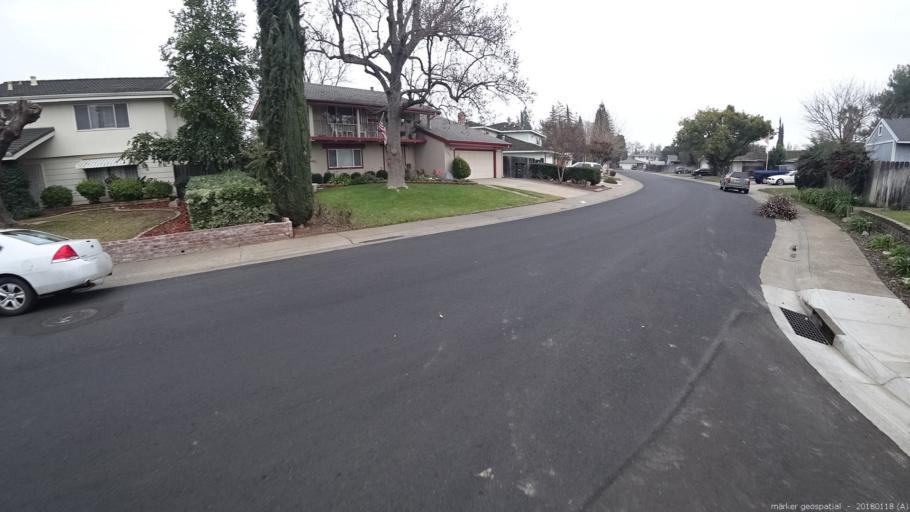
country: US
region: California
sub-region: Sacramento County
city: Rancho Cordova
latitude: 38.5890
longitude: -121.3204
